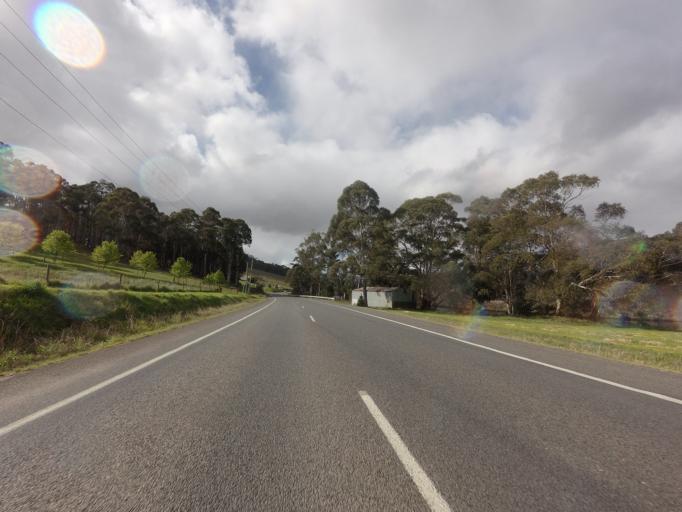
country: AU
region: Tasmania
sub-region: Huon Valley
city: Huonville
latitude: -43.0599
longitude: 147.0288
